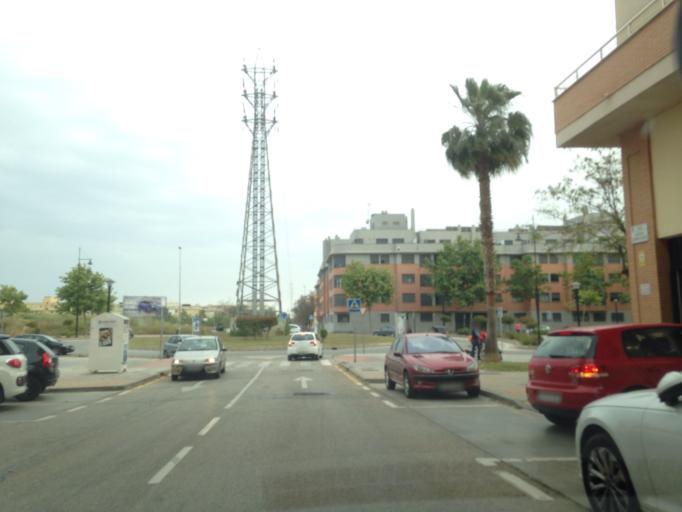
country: ES
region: Andalusia
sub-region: Provincia de Malaga
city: Malaga
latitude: 36.7249
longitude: -4.4746
